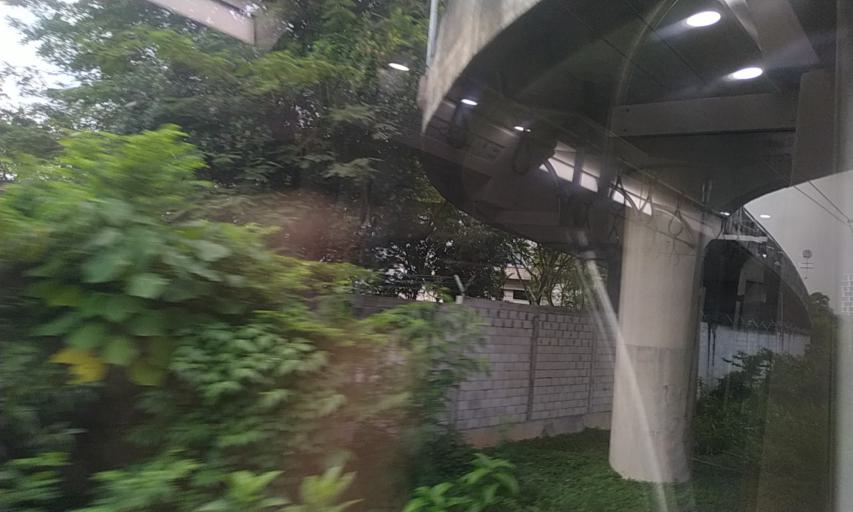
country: MY
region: Kuala Lumpur
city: Kuala Lumpur
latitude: 3.2305
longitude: 101.6744
